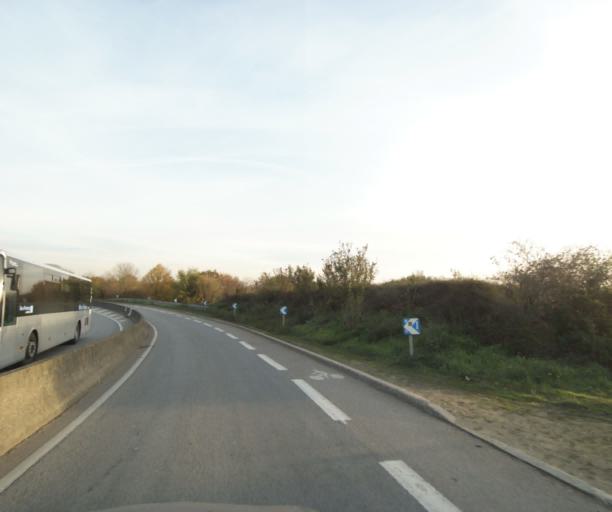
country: FR
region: Ile-de-France
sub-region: Departement des Yvelines
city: Triel-sur-Seine
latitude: 48.9718
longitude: 2.0182
